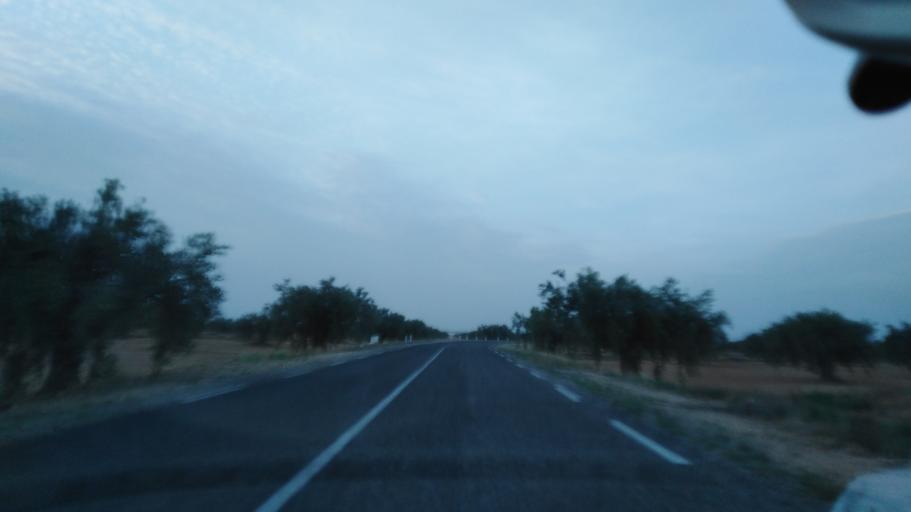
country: TN
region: Safaqis
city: Bi'r `Ali Bin Khalifah
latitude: 34.9305
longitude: 10.3870
